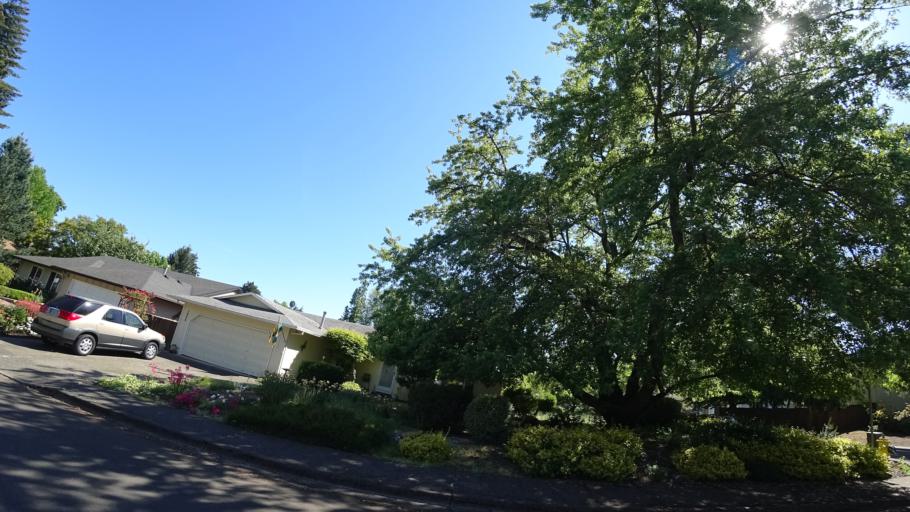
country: US
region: Oregon
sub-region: Washington County
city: Beaverton
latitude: 45.4591
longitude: -122.8028
